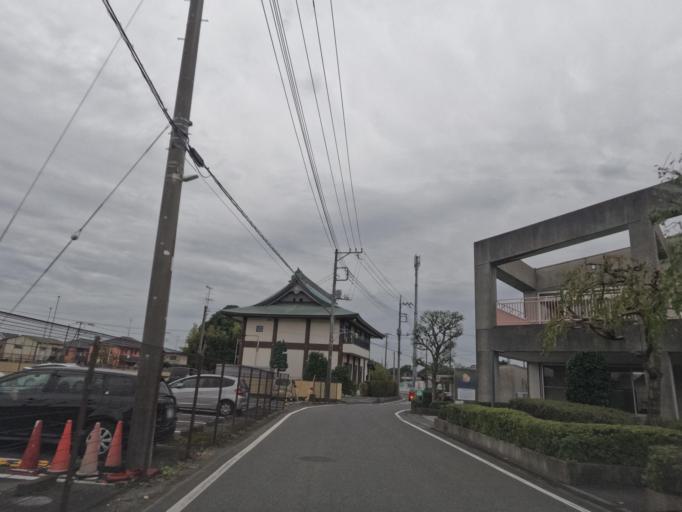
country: JP
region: Saitama
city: Saitama
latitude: 35.8890
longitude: 139.7064
